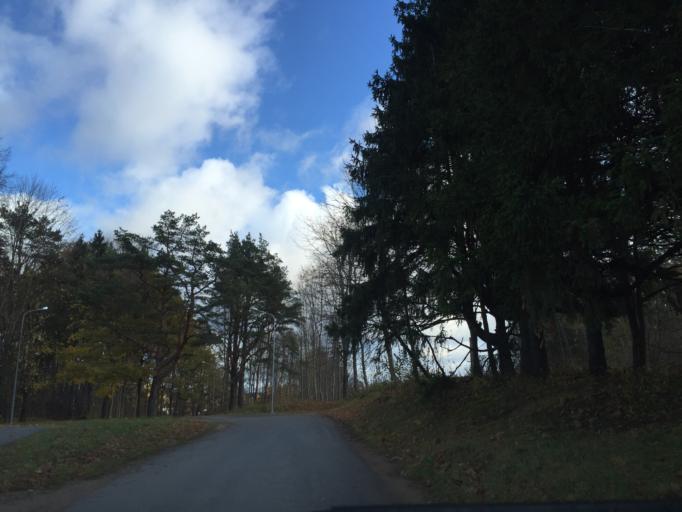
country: LV
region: Tukuma Rajons
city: Tukums
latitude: 56.9718
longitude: 23.1956
